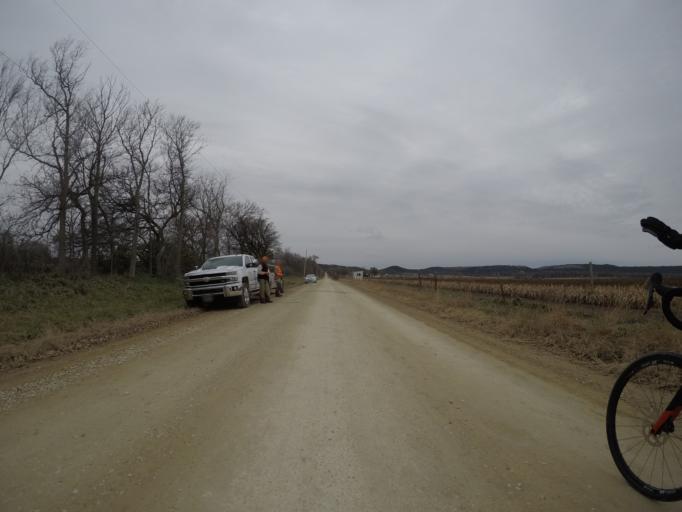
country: US
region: Kansas
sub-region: Riley County
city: Ogden
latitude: 39.1549
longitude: -96.6819
